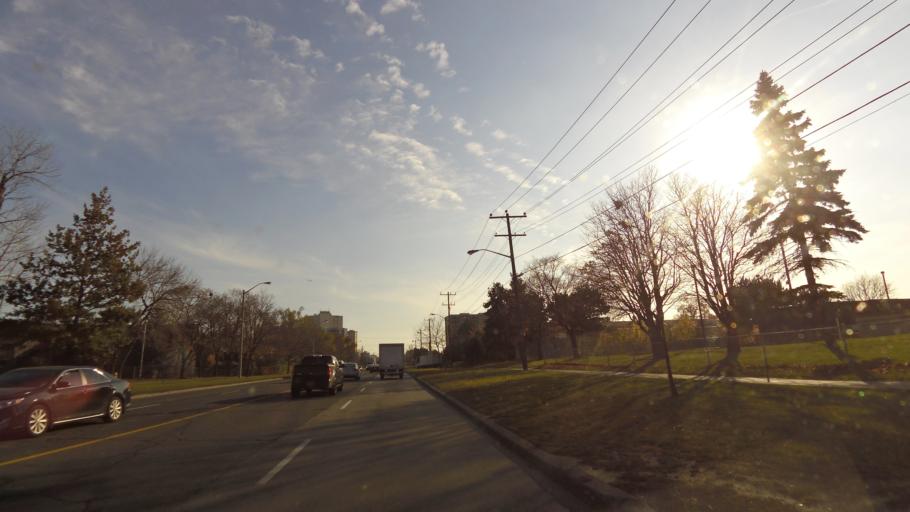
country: CA
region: Ontario
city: Concord
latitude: 43.7651
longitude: -79.5196
